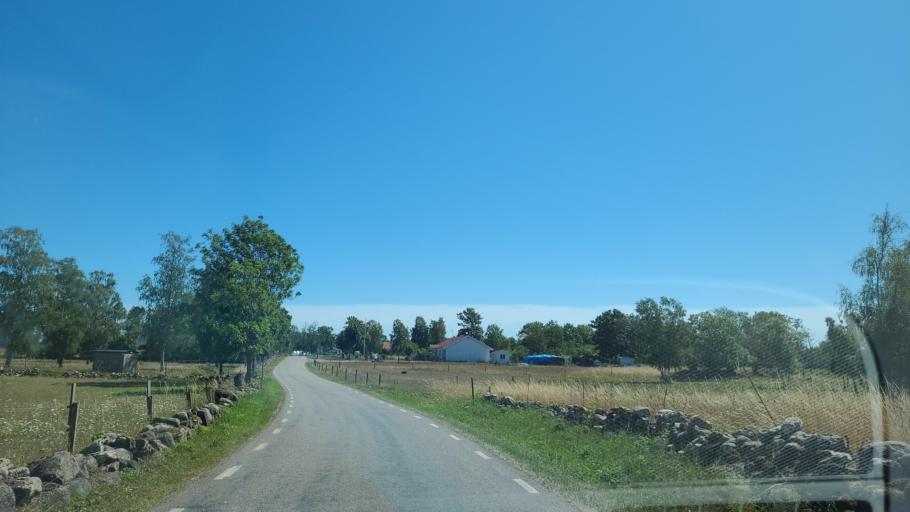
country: SE
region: Kalmar
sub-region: Borgholms Kommun
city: Borgholm
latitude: 56.7456
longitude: 16.6947
